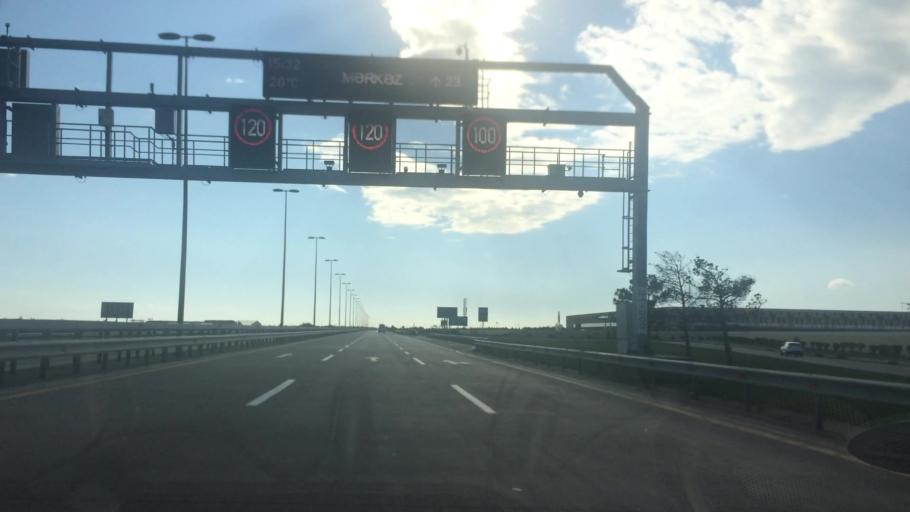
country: AZ
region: Baki
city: Hovsan
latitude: 40.3874
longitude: 50.0672
